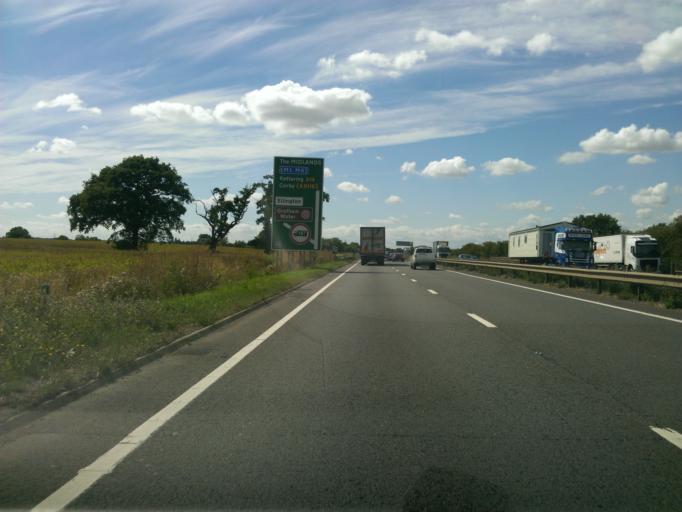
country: GB
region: England
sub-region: Cambridgeshire
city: Buckden
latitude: 52.3323
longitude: -0.2765
